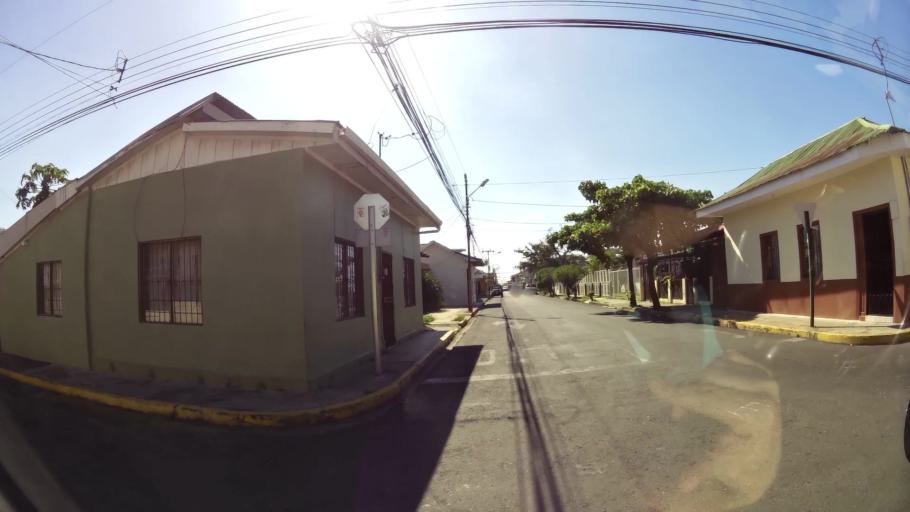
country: CR
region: Guanacaste
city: Liberia
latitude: 10.6314
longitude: -85.4337
